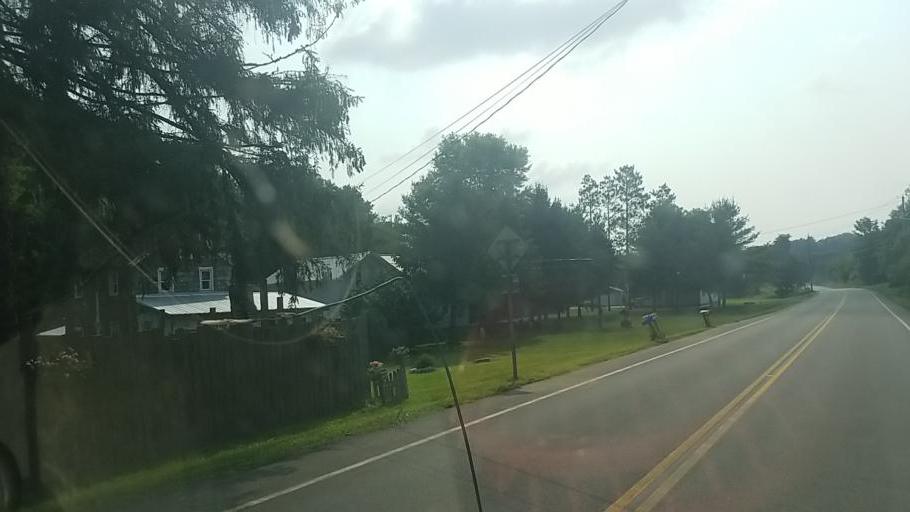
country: US
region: New York
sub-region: Montgomery County
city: Fonda
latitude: 42.9628
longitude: -74.4163
